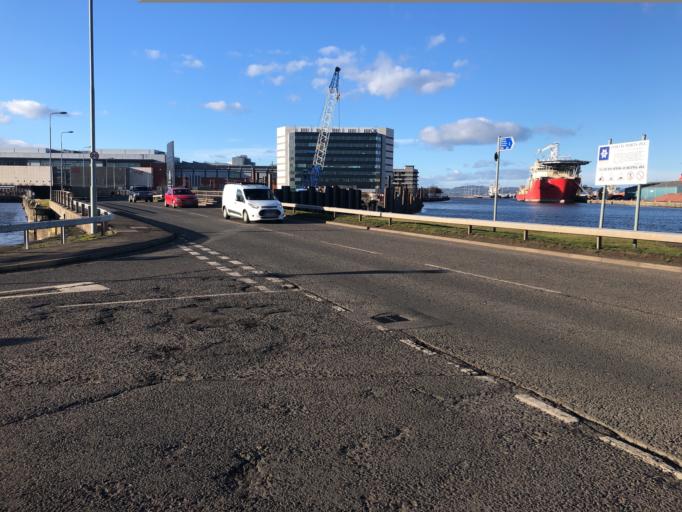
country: GB
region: Scotland
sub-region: West Lothian
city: Seafield
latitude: 55.9792
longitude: -3.1714
